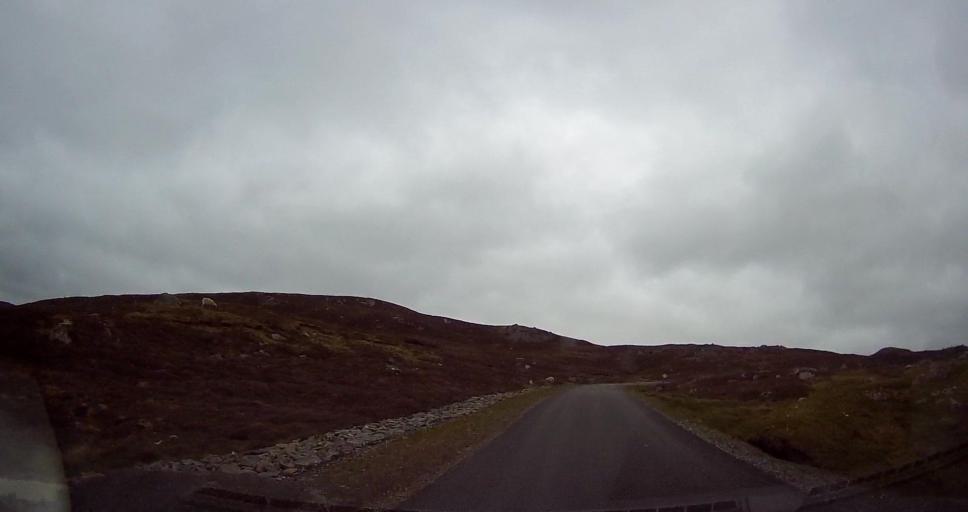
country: GB
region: Scotland
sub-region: Shetland Islands
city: Lerwick
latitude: 60.3403
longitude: -1.3167
